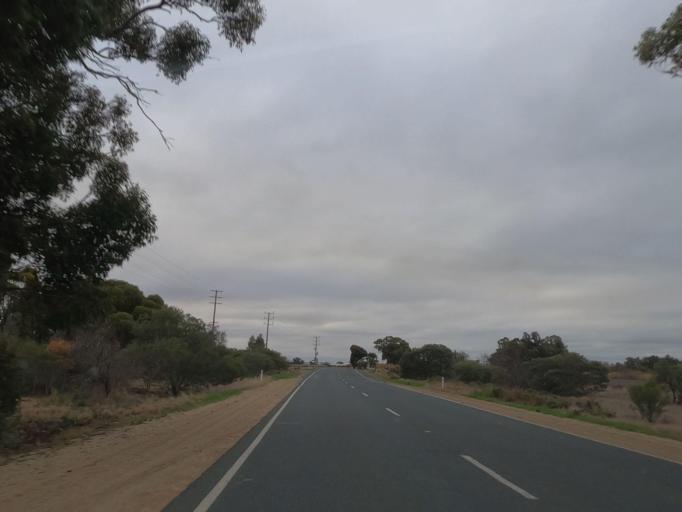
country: AU
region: Victoria
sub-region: Swan Hill
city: Swan Hill
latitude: -35.3963
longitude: 143.5735
